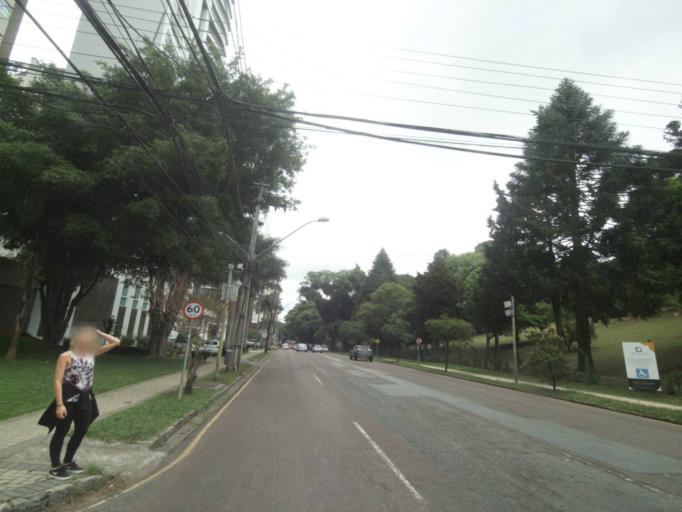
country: BR
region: Parana
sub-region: Curitiba
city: Curitiba
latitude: -25.4325
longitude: -49.3017
